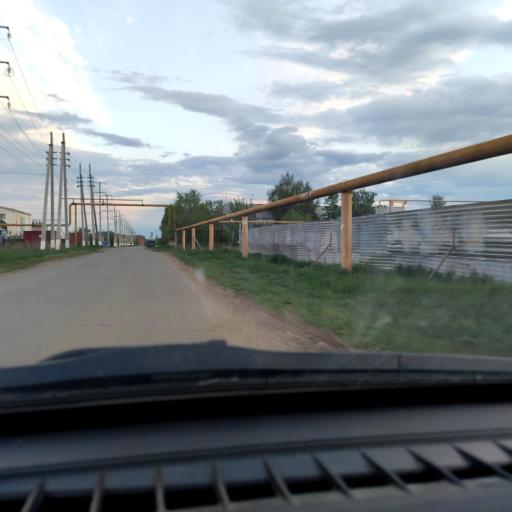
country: RU
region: Samara
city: Podstepki
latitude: 53.5203
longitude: 49.1129
